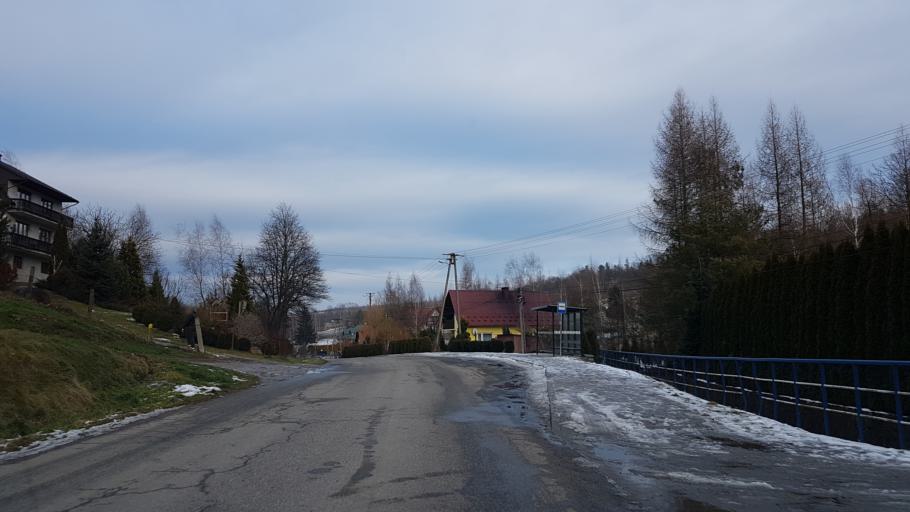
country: PL
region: Lesser Poland Voivodeship
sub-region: Powiat nowosadecki
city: Stary Sacz
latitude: 49.5330
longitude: 20.6083
